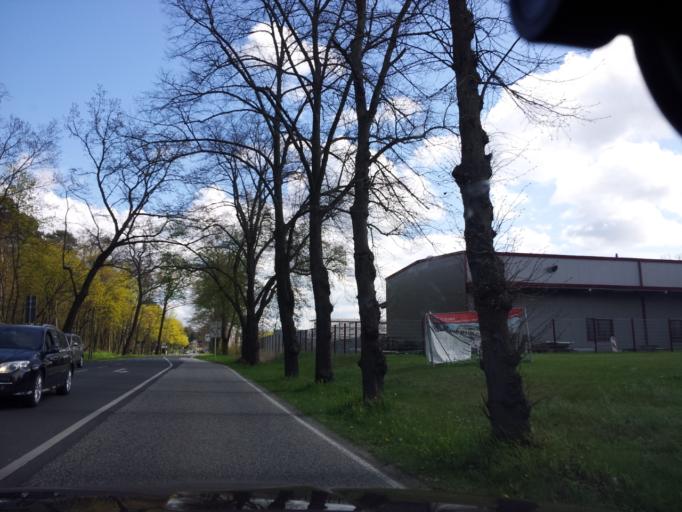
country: DE
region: Brandenburg
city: Bernau bei Berlin
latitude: 52.6879
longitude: 13.5667
